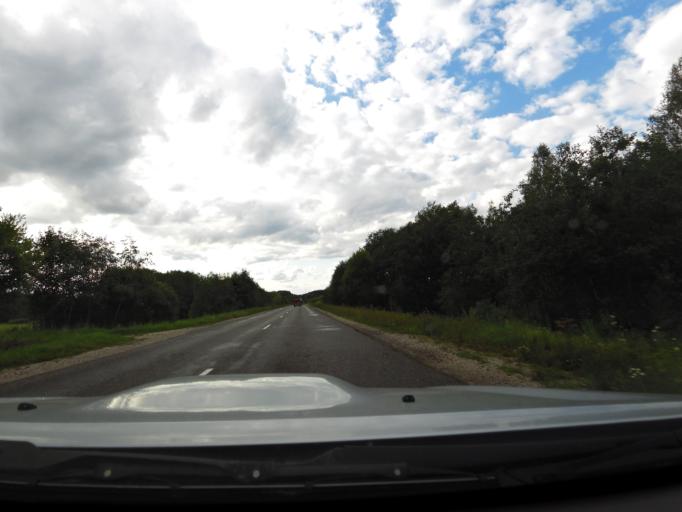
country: LV
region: Akniste
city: Akniste
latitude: 55.9998
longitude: 25.9591
